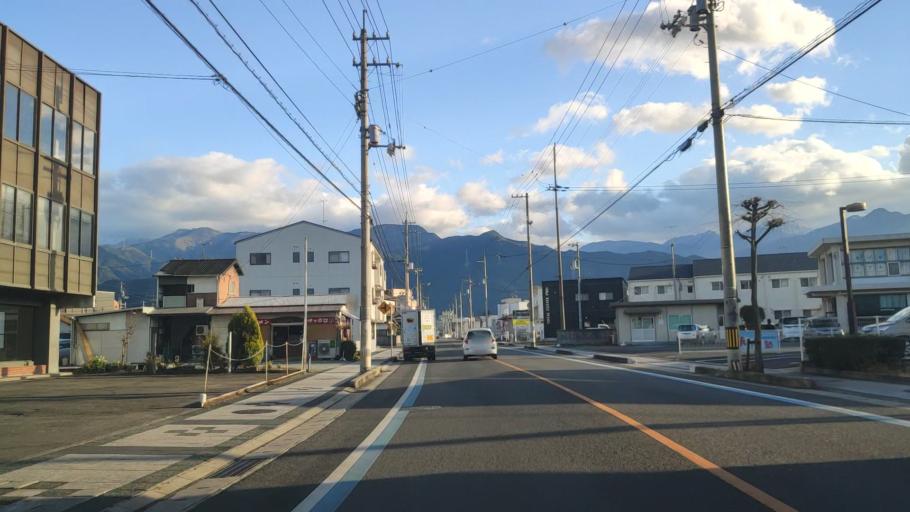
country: JP
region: Ehime
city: Saijo
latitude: 33.9143
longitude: 133.1781
